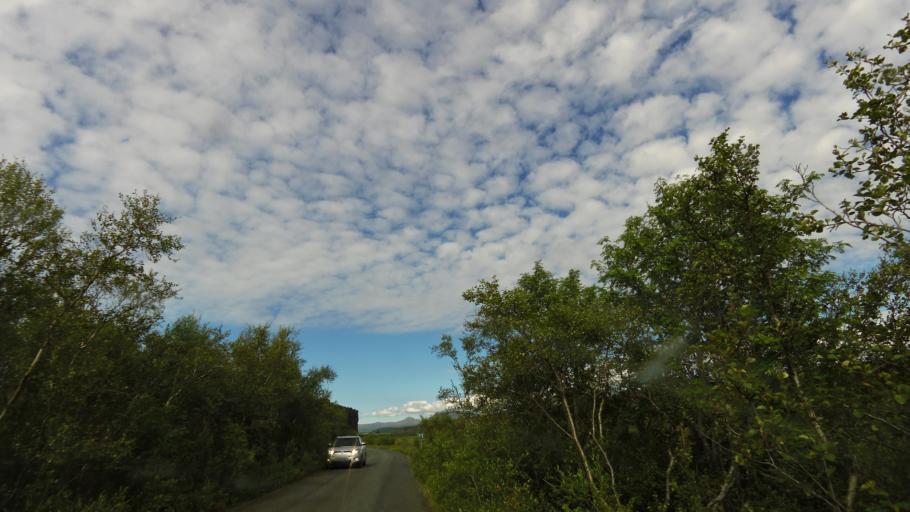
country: IS
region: Northeast
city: Husavik
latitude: 66.0067
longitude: -16.5091
